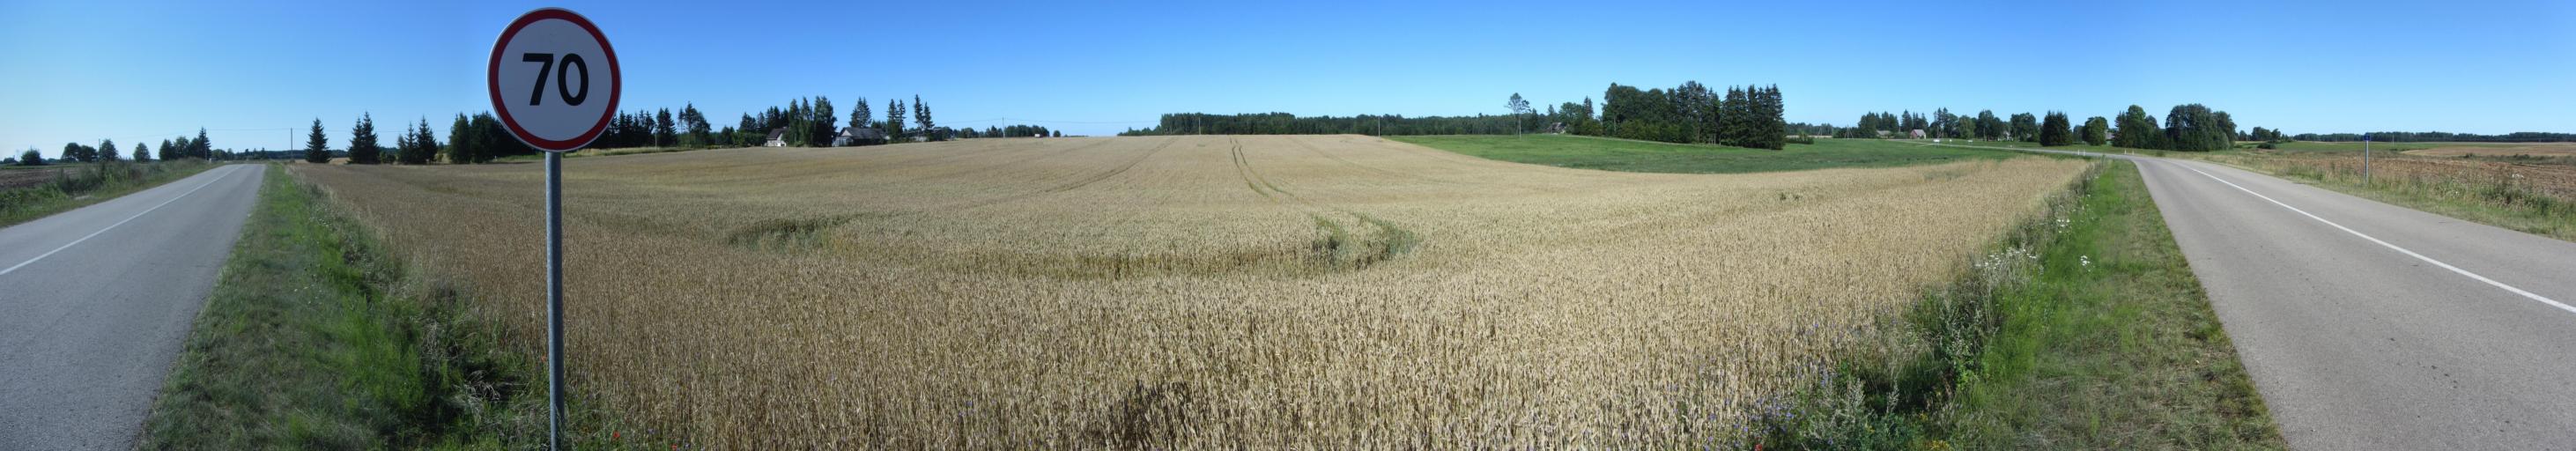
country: LT
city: Obeliai
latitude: 55.8167
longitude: 25.1234
